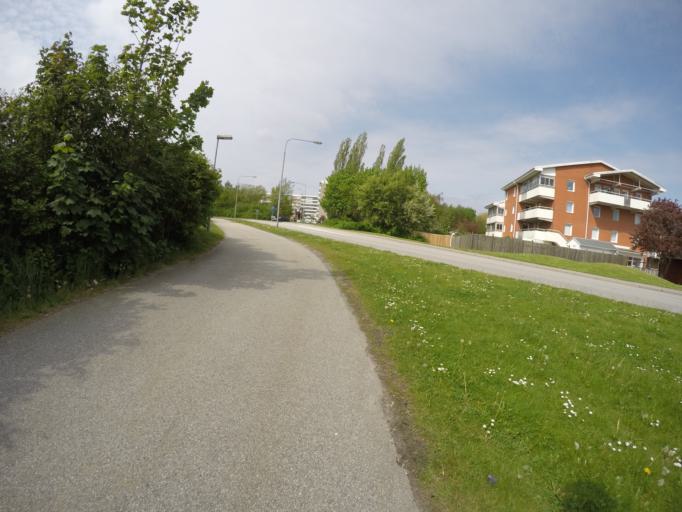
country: SE
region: Skane
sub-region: Malmo
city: Tygelsjo
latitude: 55.5559
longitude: 12.9914
